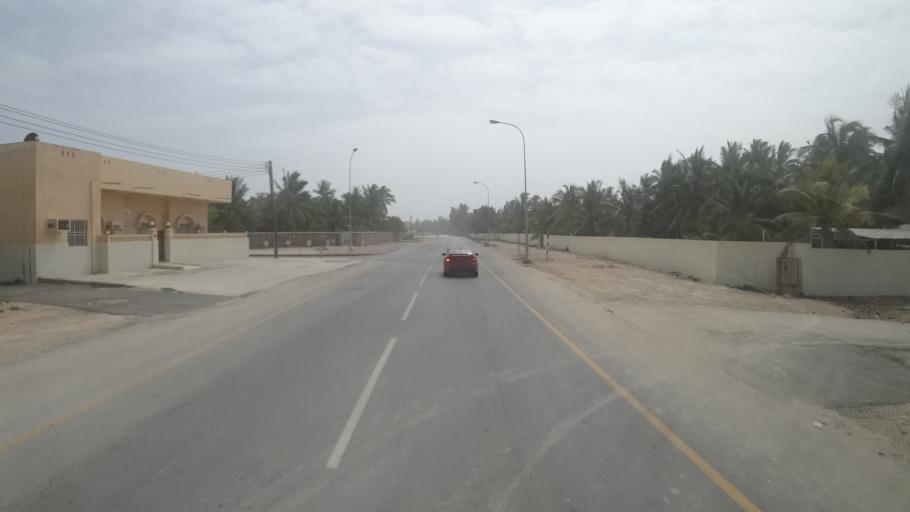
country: OM
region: Zufar
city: Salalah
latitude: 17.0116
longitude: 54.1579
